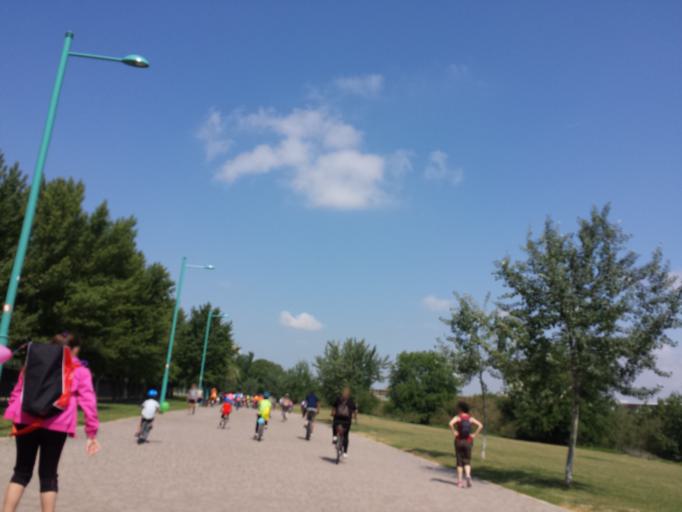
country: ES
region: Aragon
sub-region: Provincia de Zaragoza
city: Almozara
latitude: 41.6646
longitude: -0.8965
